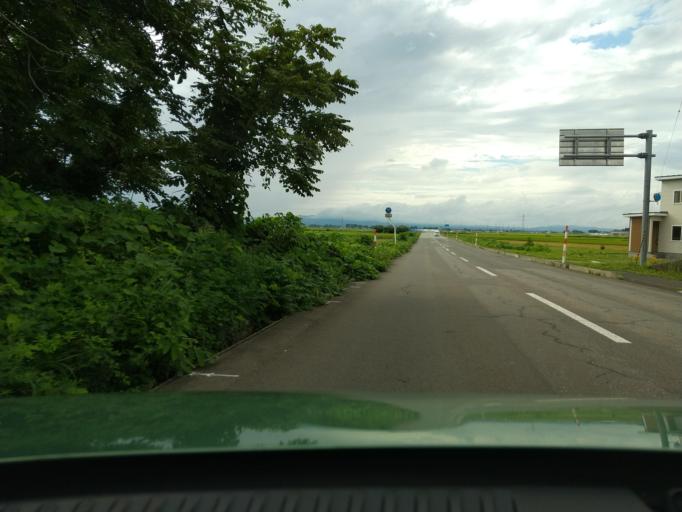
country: JP
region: Akita
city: Yuzawa
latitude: 39.2352
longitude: 140.5092
